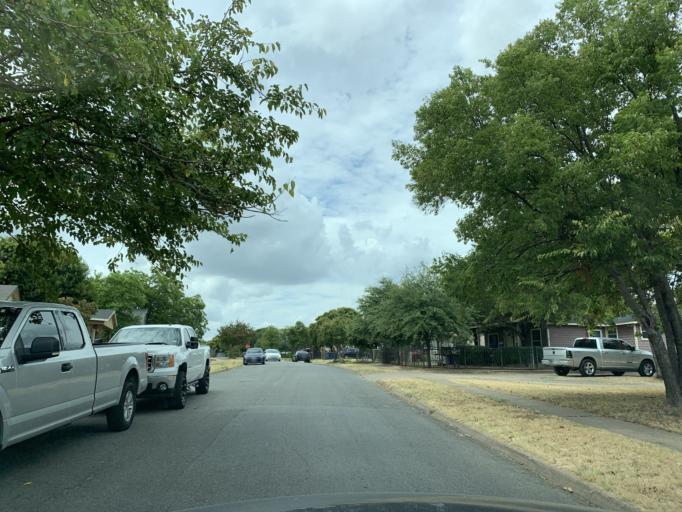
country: US
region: Texas
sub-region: Dallas County
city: Cockrell Hill
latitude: 32.7452
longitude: -96.8792
